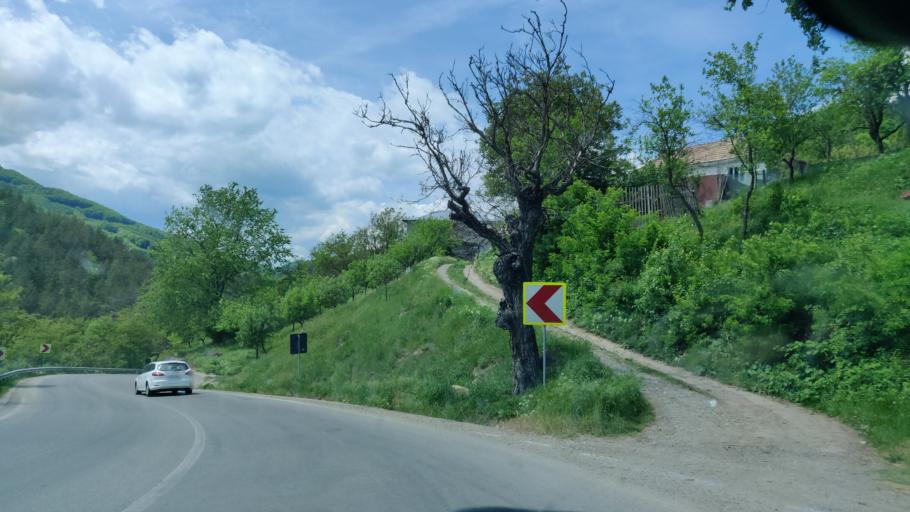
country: RO
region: Vrancea
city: Matacina
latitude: 45.8892
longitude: 26.8136
